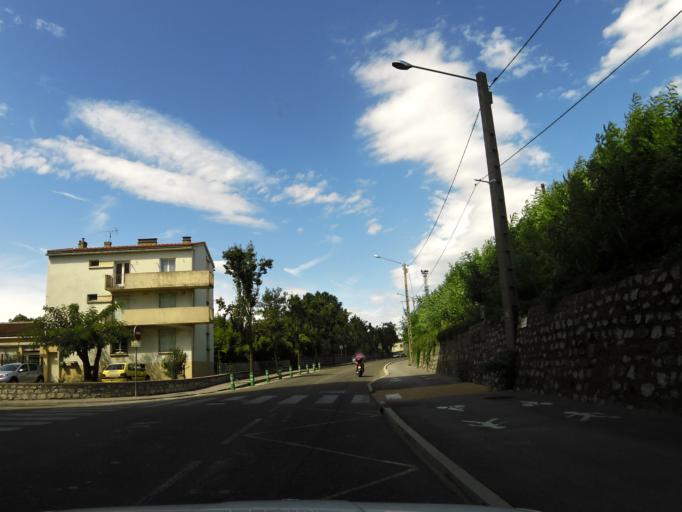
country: FR
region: Languedoc-Roussillon
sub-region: Departement du Gard
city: Ales
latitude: 44.1236
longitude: 4.0916
